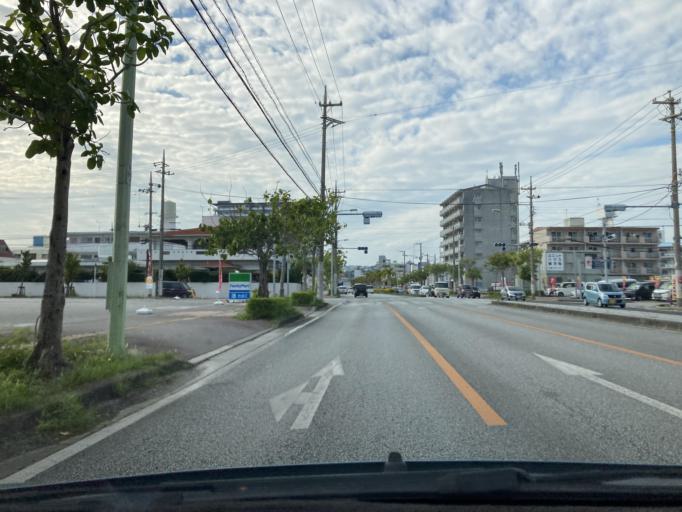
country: JP
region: Okinawa
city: Okinawa
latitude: 26.3168
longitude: 127.8282
